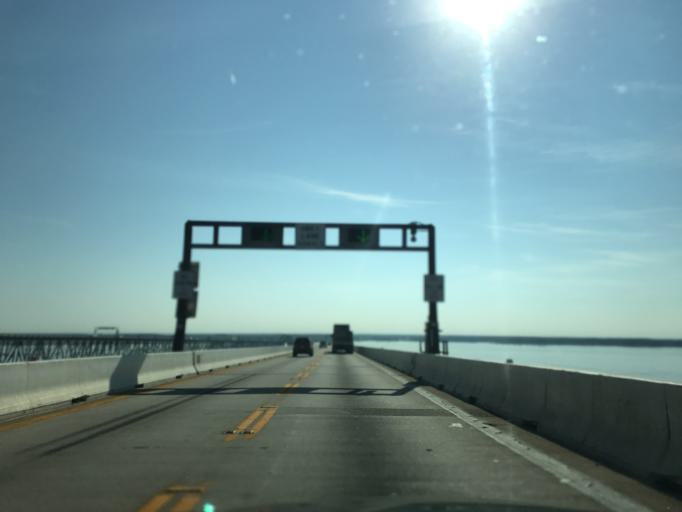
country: US
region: Maryland
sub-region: Queen Anne's County
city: Stevensville
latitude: 38.9917
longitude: -76.3760
